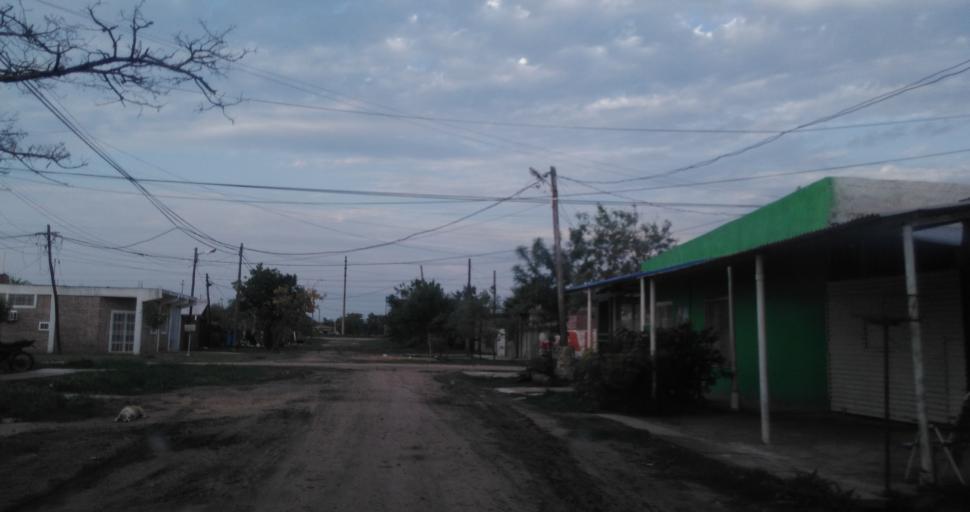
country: AR
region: Chaco
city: Resistencia
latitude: -27.4793
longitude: -59.0019
